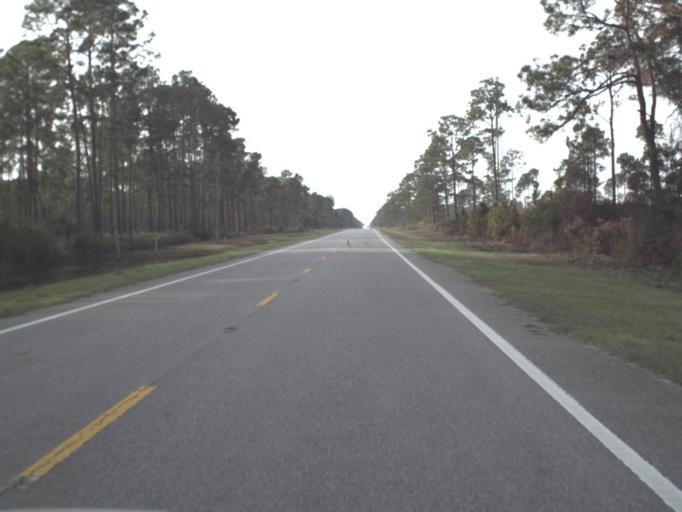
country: US
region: Florida
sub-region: Bay County
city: Mexico Beach
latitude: 29.9930
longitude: -85.4903
